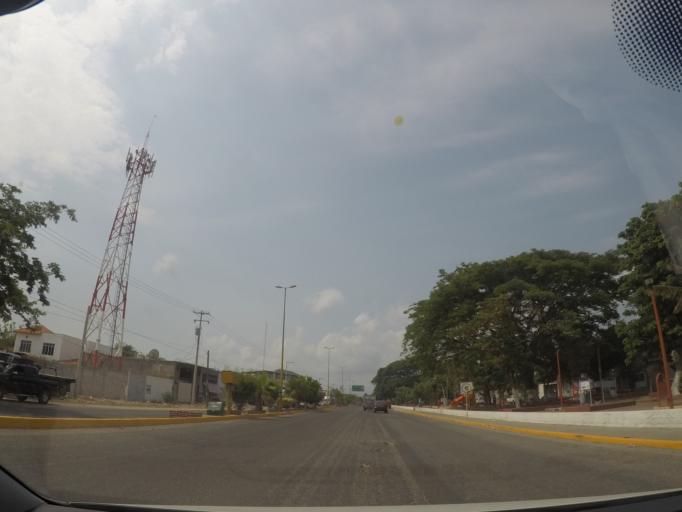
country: MX
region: Oaxaca
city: Juchitan de Zaragoza
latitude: 16.4507
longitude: -95.0267
